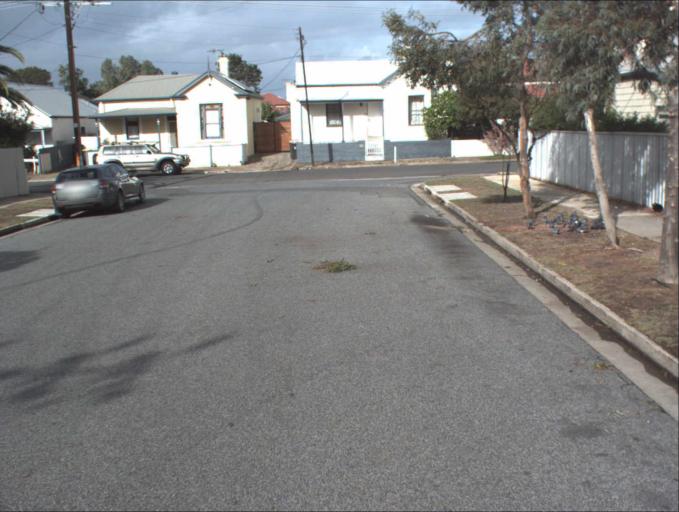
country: AU
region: South Australia
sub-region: Port Adelaide Enfield
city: Birkenhead
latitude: -34.8415
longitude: 138.4866
